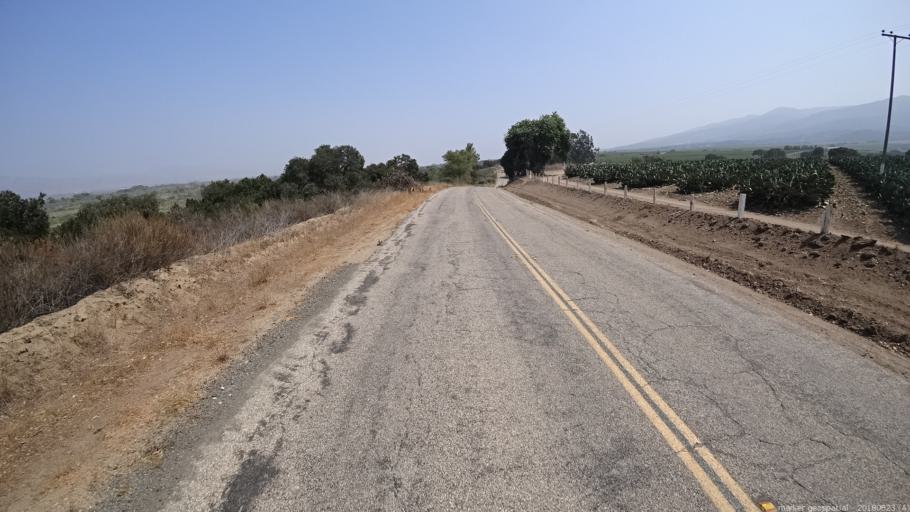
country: US
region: California
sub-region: Monterey County
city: Gonzales
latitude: 36.4494
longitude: -121.4357
